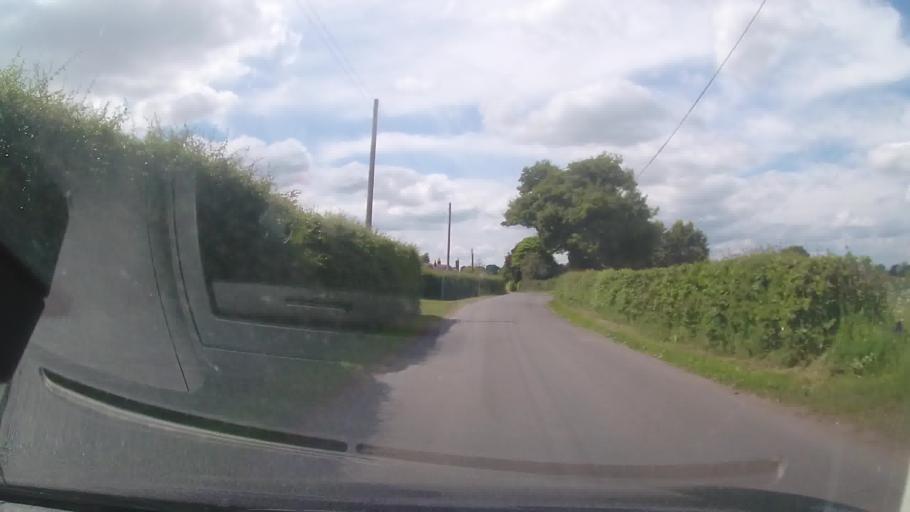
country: GB
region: England
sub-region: Shropshire
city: Stoke upon Tern
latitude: 52.7934
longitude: -2.5572
